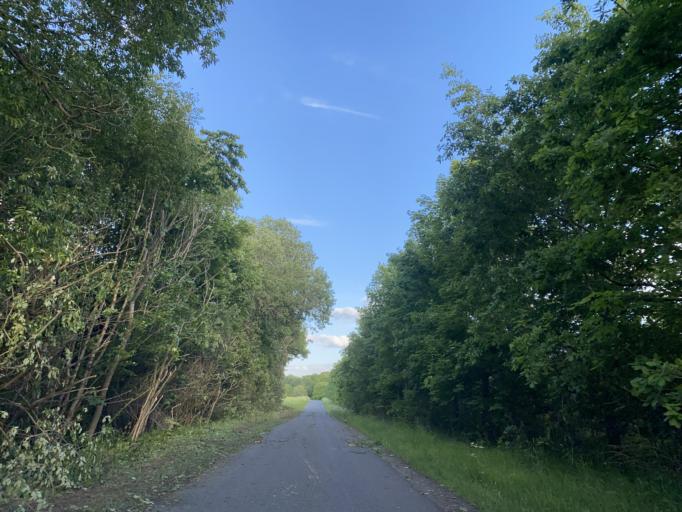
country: DK
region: Central Jutland
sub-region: Viborg Kommune
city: Bjerringbro
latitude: 56.3244
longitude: 9.6621
